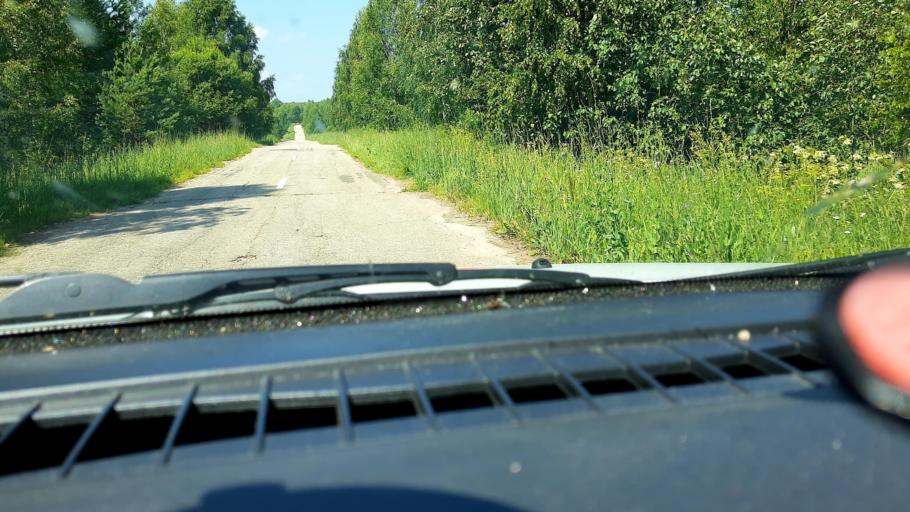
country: RU
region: Nizjnij Novgorod
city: Sharanga
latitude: 57.0530
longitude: 46.7098
